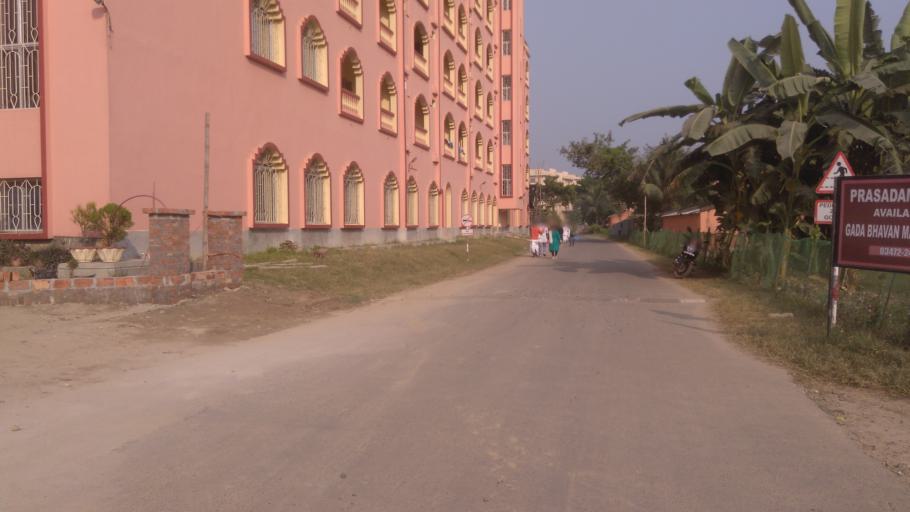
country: IN
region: West Bengal
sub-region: Nadia
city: Navadwip
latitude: 23.4267
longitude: 88.3890
